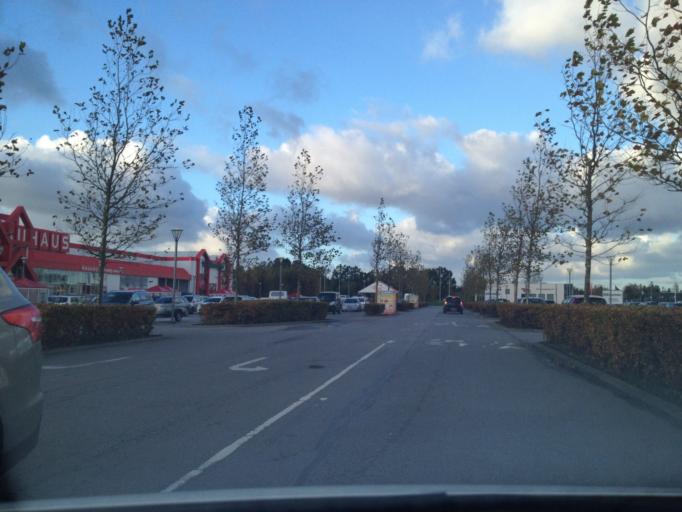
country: DK
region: Capital Region
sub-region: Hillerod Kommune
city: Hillerod
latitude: 55.9329
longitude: 12.2605
